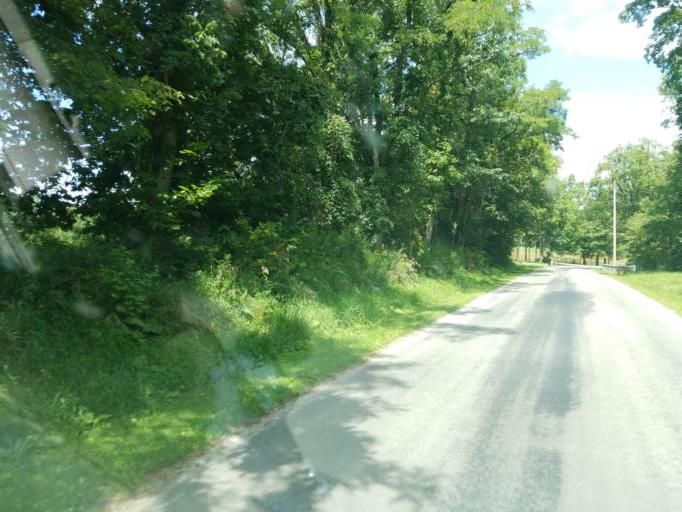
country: US
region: Ohio
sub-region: Delaware County
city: Sunbury
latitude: 40.2651
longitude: -82.8430
